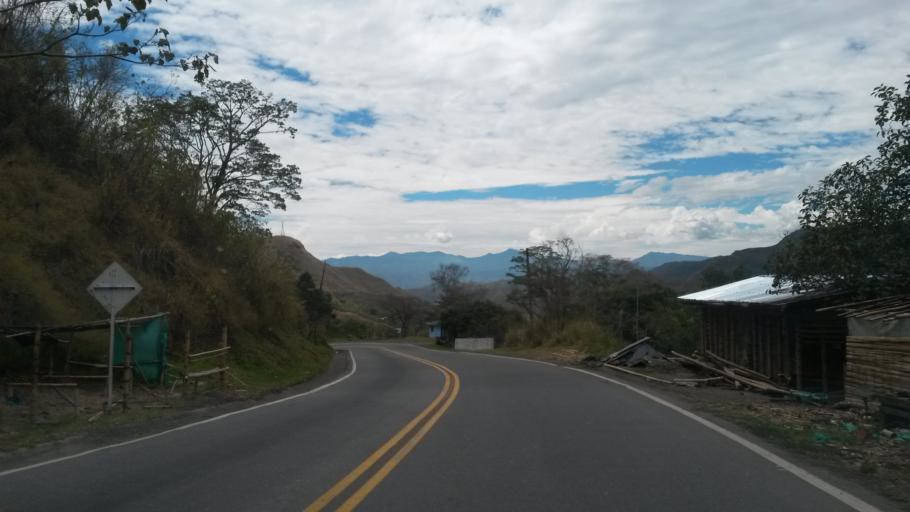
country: CO
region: Cauca
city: Rosas
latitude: 2.2774
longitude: -76.7229
